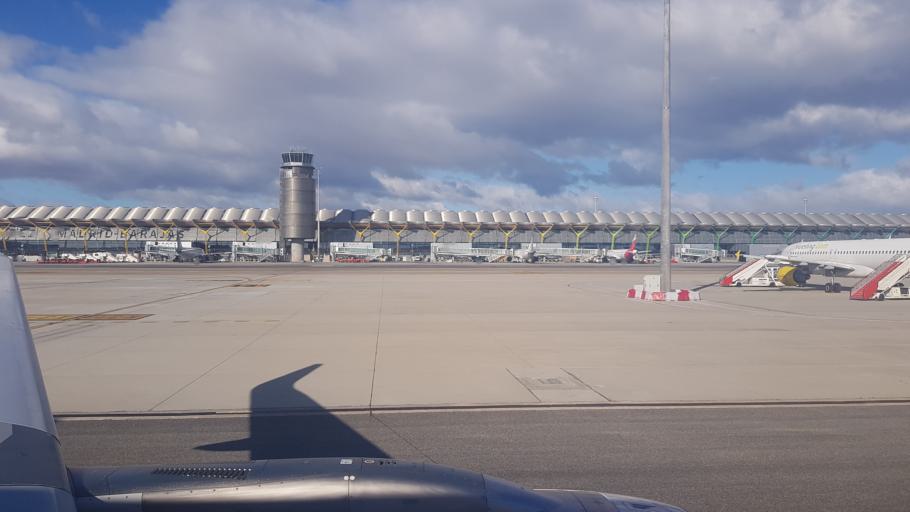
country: ES
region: Madrid
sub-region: Provincia de Madrid
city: Barajas de Madrid
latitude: 40.4925
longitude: -3.5865
